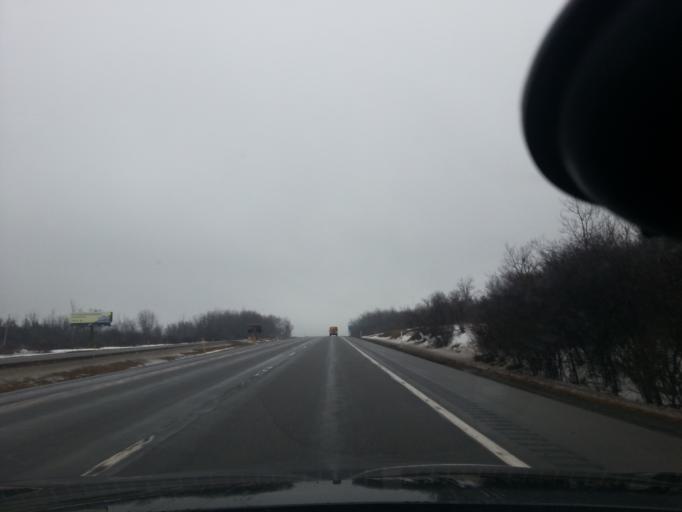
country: US
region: New York
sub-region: Jefferson County
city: Watertown
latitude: 43.9501
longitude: -75.9562
